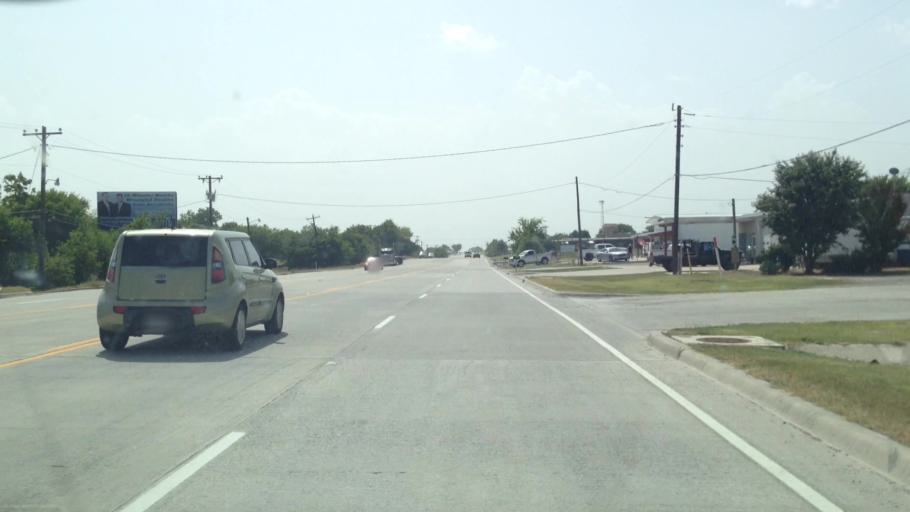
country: US
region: Texas
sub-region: Collin County
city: Farmersville
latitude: 33.1570
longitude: -96.3684
